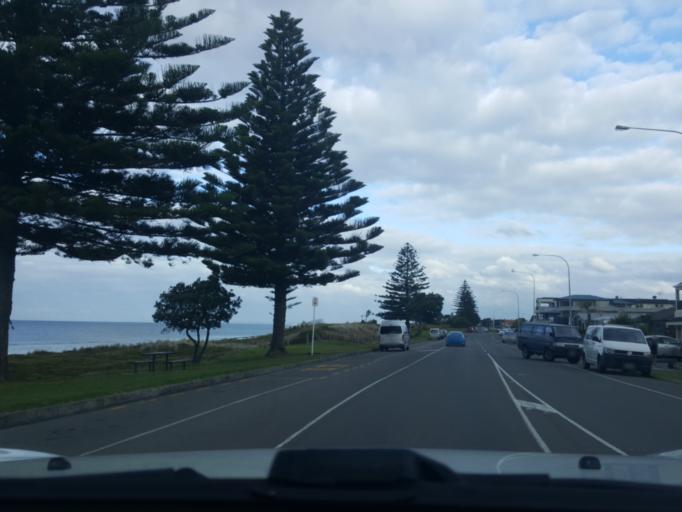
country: NZ
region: Bay of Plenty
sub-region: Tauranga City
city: Tauranga
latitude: -37.6499
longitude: 176.2026
